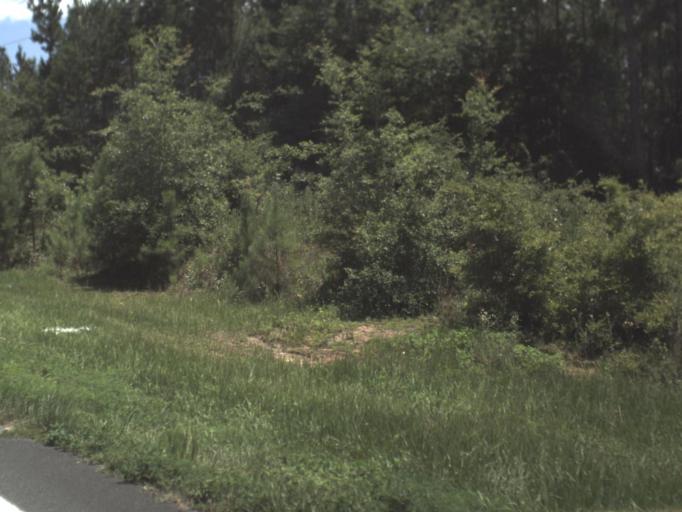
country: US
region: Florida
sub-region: Alachua County
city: Hawthorne
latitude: 29.6440
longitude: -82.0328
